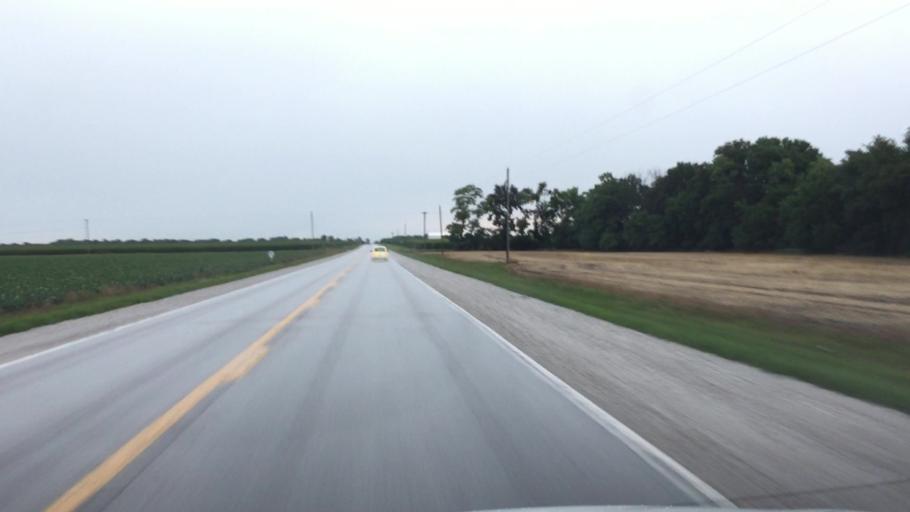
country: US
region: Illinois
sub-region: Hancock County
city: Carthage
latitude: 40.4440
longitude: -91.1399
